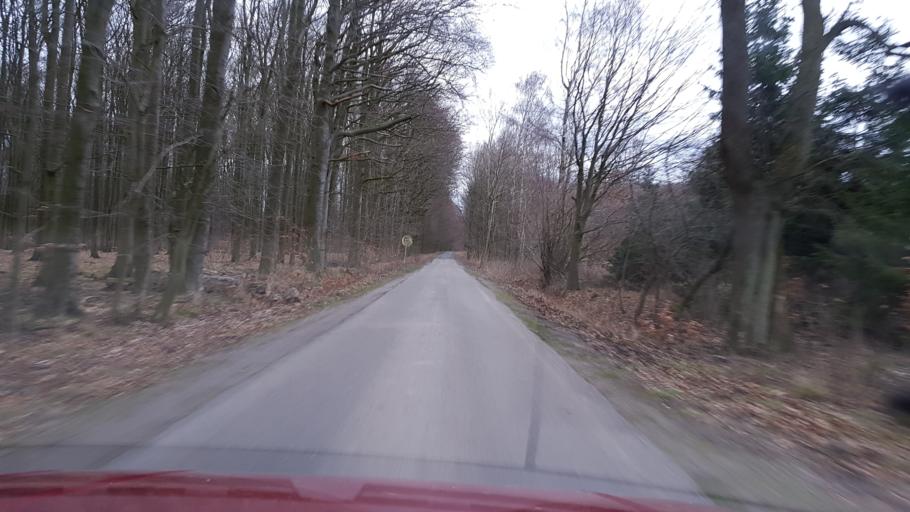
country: PL
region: West Pomeranian Voivodeship
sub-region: Powiat gryfinski
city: Stare Czarnowo
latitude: 53.3218
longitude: 14.7071
